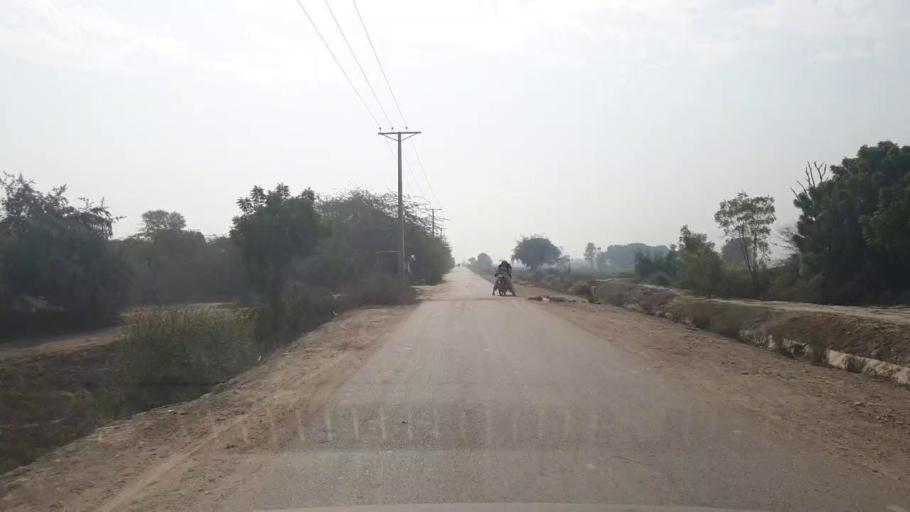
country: PK
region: Sindh
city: Hala
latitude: 25.7832
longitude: 68.4425
